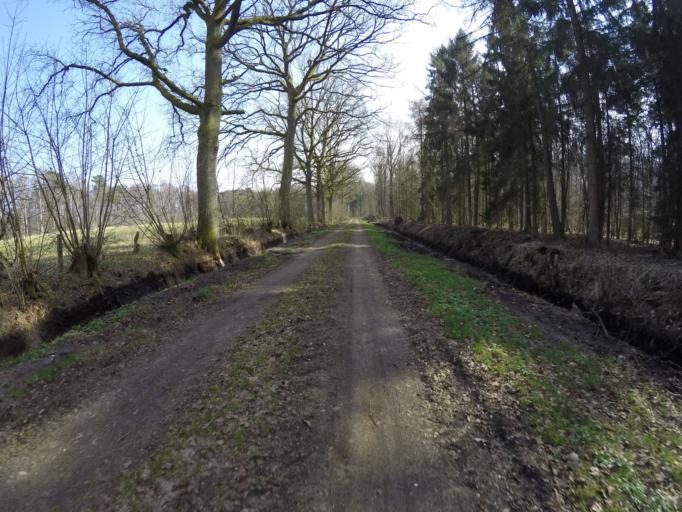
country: DE
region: Schleswig-Holstein
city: Borstel-Hohenraden
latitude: 53.7238
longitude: 9.8267
